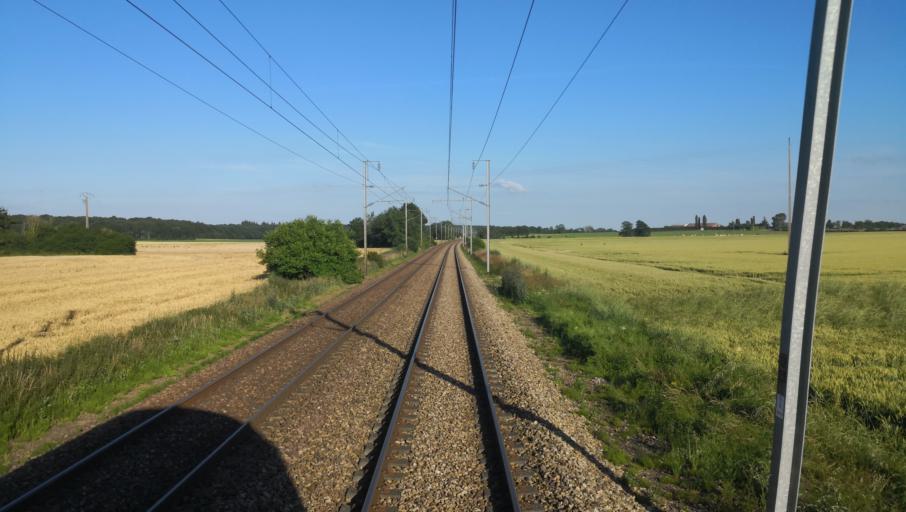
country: FR
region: Haute-Normandie
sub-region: Departement de l'Eure
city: Conches-en-Ouche
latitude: 48.9948
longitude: 0.8738
